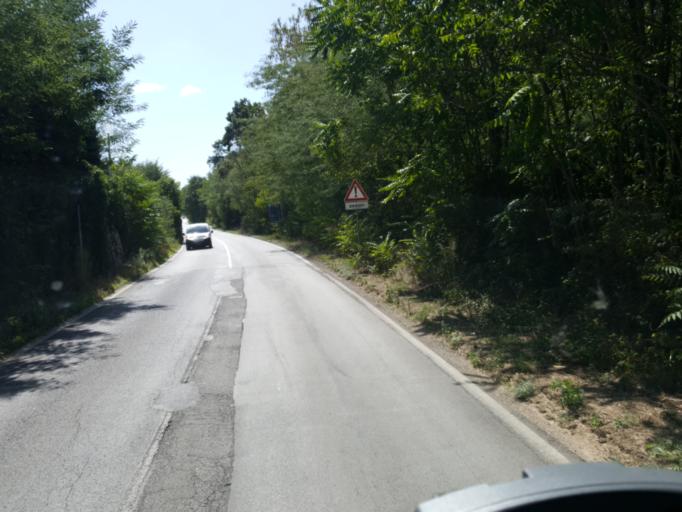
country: IT
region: Latium
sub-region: Provincia di Latina
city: Priverno
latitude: 41.4365
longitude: 13.1916
